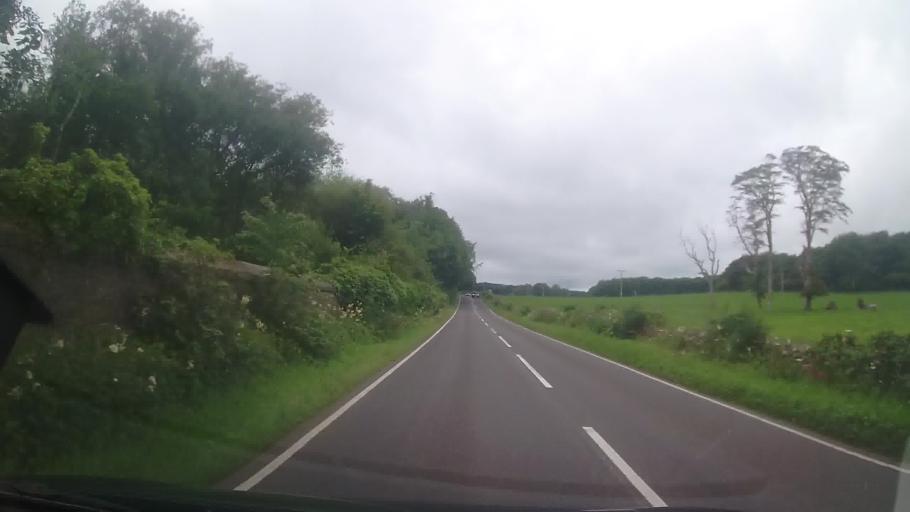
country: GB
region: Wales
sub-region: Anglesey
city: Llanfairpwllgwyngyll
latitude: 53.2114
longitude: -4.2149
